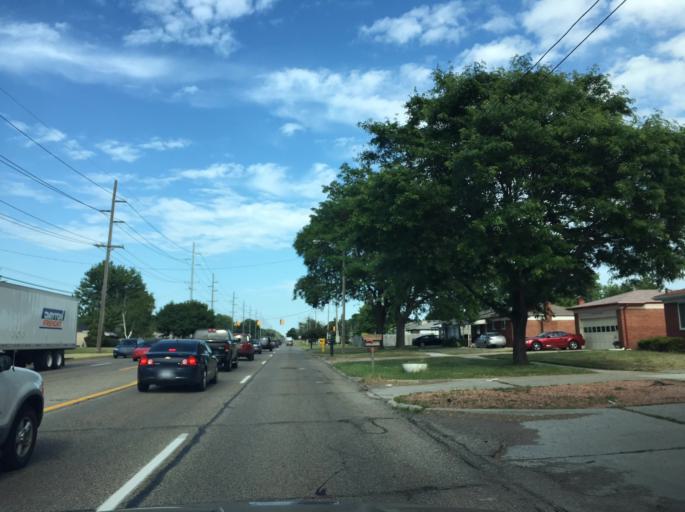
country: US
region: Michigan
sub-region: Macomb County
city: Fraser
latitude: 42.5381
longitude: -82.9809
